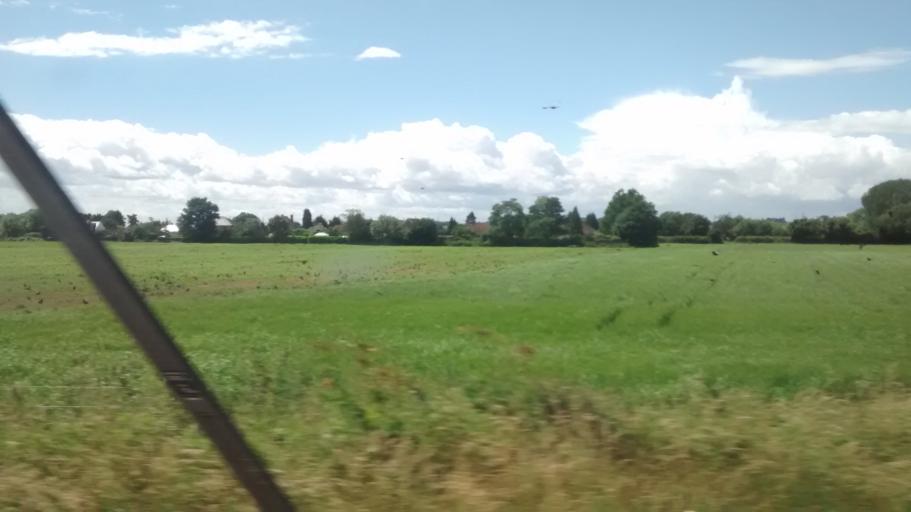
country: GB
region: England
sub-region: Nottinghamshire
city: Newark on Trent
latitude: 53.1117
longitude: -0.8168
